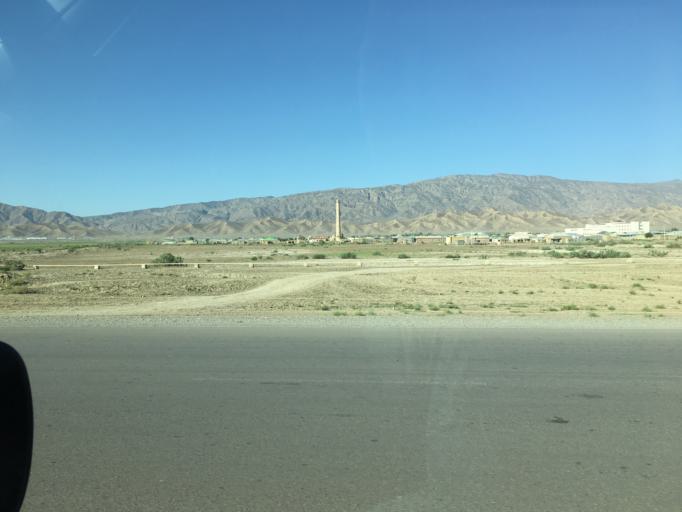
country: TM
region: Ahal
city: Baharly
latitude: 38.3775
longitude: 57.5064
